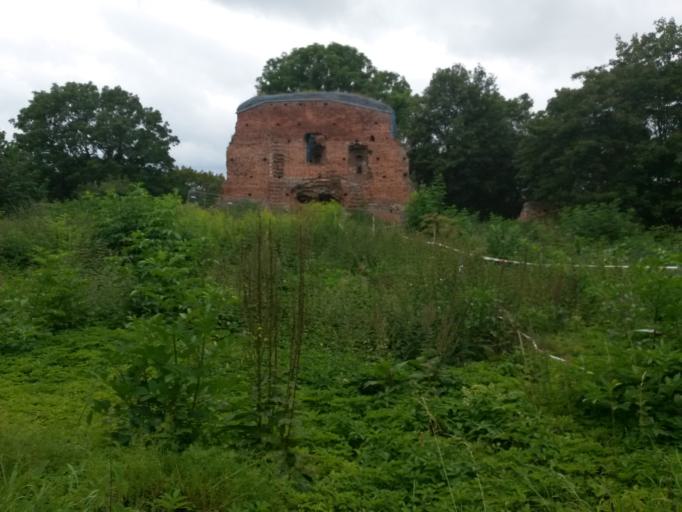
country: DE
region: Brandenburg
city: Angermunde
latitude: 53.0913
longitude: 13.9649
